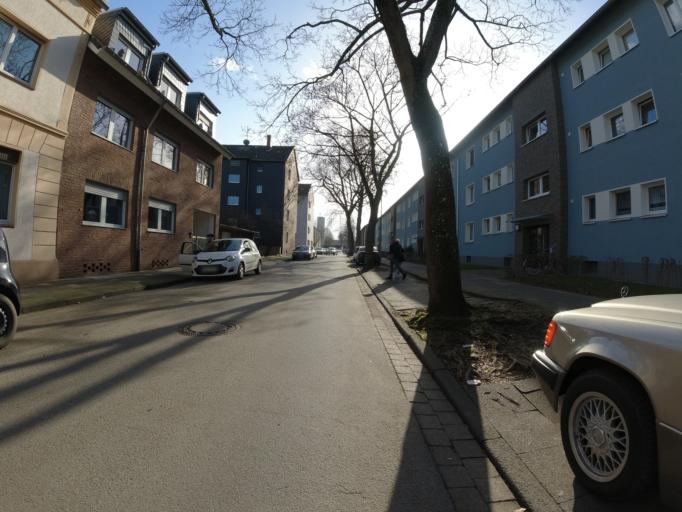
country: DE
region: North Rhine-Westphalia
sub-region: Regierungsbezirk Dusseldorf
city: Hochfeld
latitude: 51.4023
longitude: 6.7007
